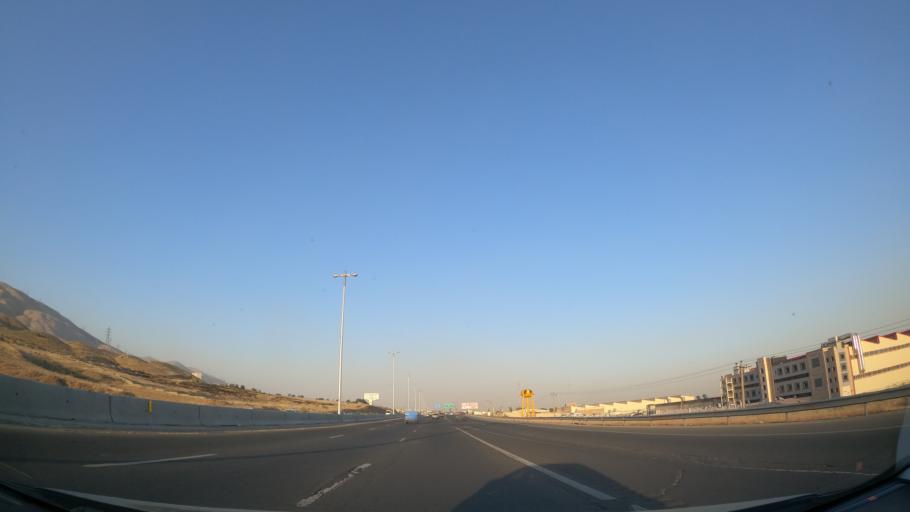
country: IR
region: Tehran
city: Shahr-e Qods
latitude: 35.7427
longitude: 51.1074
